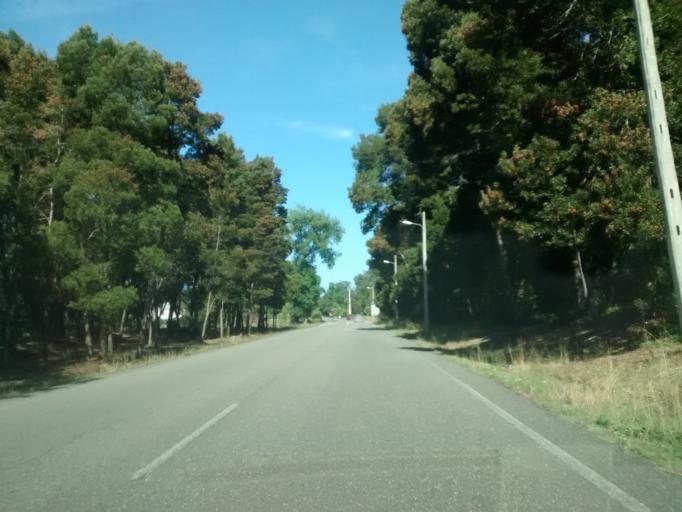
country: PT
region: Coimbra
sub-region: Mira
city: Mira
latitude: 40.4531
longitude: -8.7762
